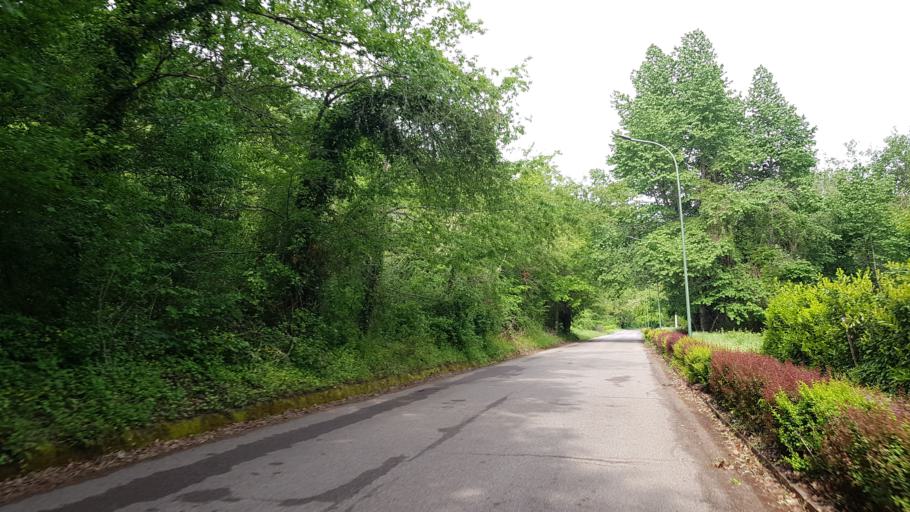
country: IT
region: Basilicate
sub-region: Provincia di Potenza
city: Rionero in Vulture
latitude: 40.9262
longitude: 15.6055
